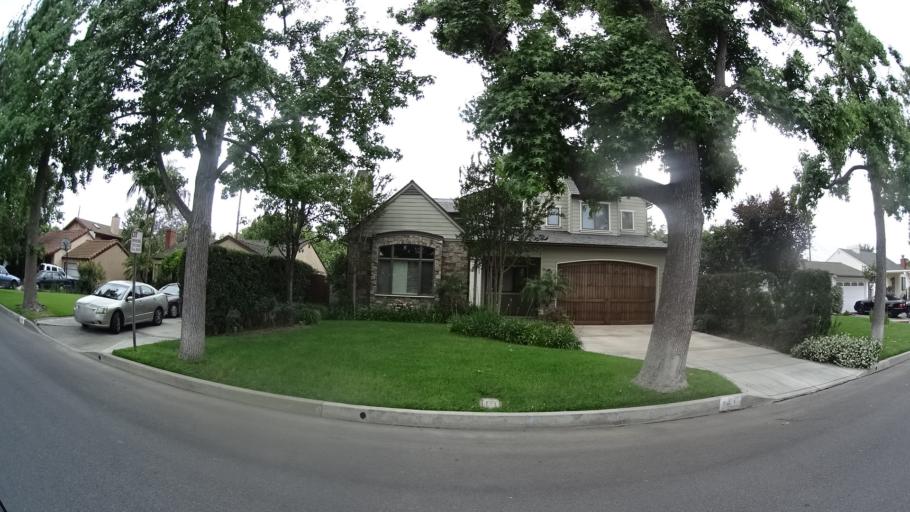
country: US
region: California
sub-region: Los Angeles County
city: Universal City
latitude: 34.1618
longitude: -118.3497
